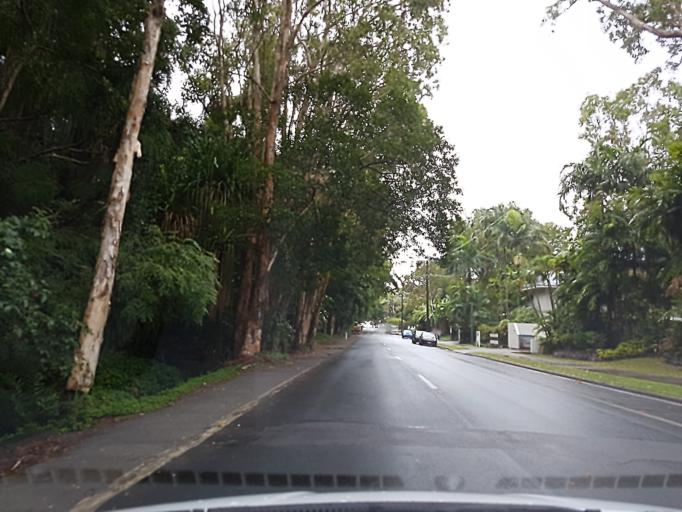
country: AU
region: Queensland
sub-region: Cairns
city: Palm Cove
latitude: -16.7430
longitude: 145.6690
